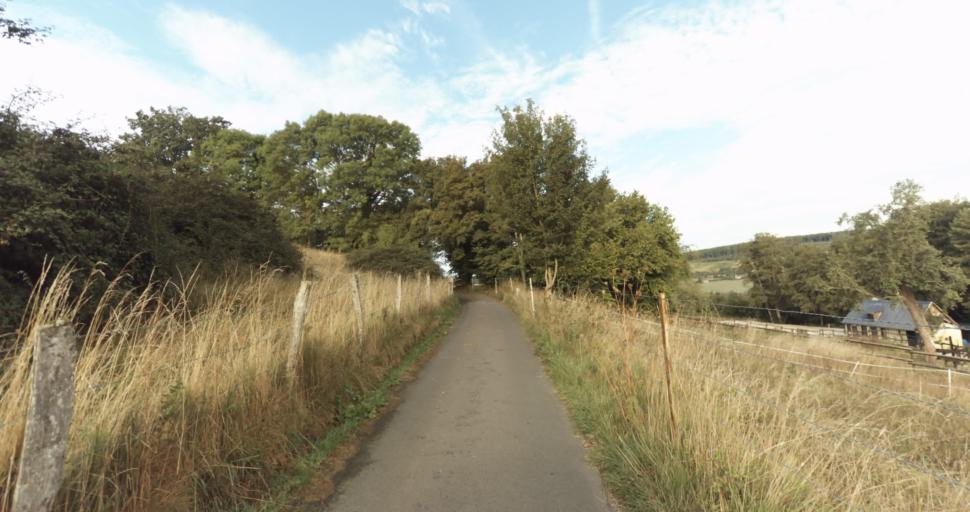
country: FR
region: Lower Normandy
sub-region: Departement de l'Orne
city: Vimoutiers
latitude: 48.8898
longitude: 0.2237
